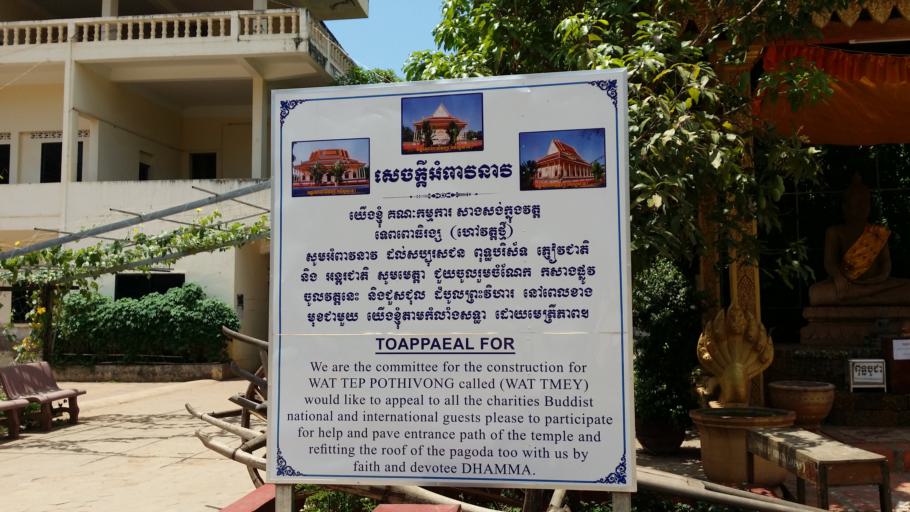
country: KH
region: Siem Reap
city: Siem Reap
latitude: 13.3829
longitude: 103.8600
